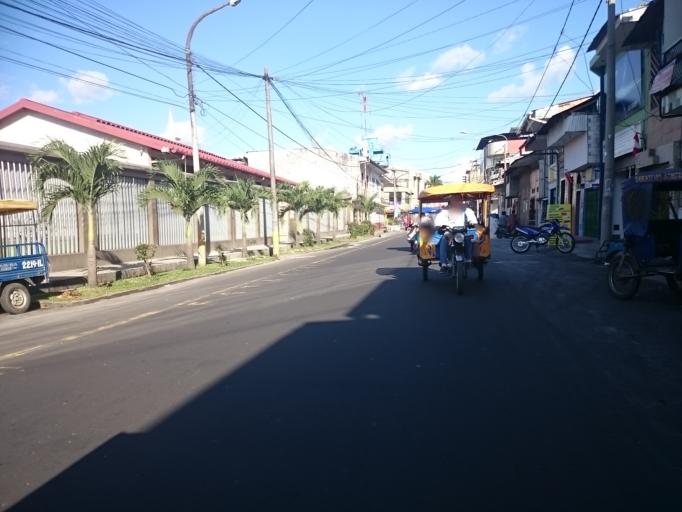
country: PE
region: Loreto
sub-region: Provincia de Maynas
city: Iquitos
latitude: -3.7474
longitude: -73.2459
